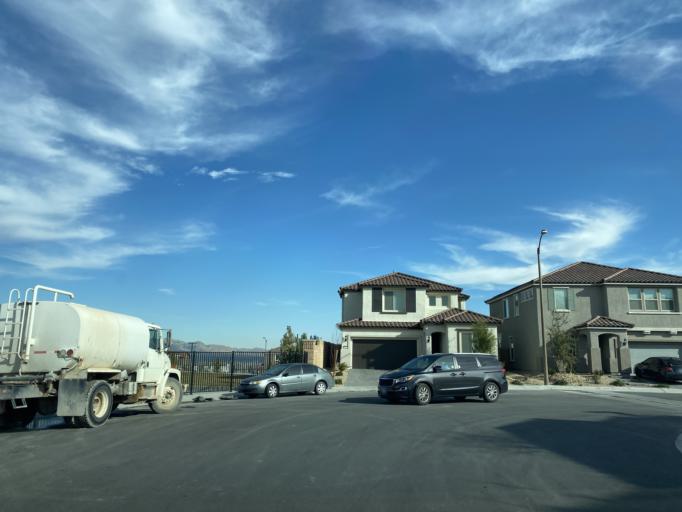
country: US
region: Nevada
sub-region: Clark County
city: Summerlin South
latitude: 36.3099
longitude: -115.3253
